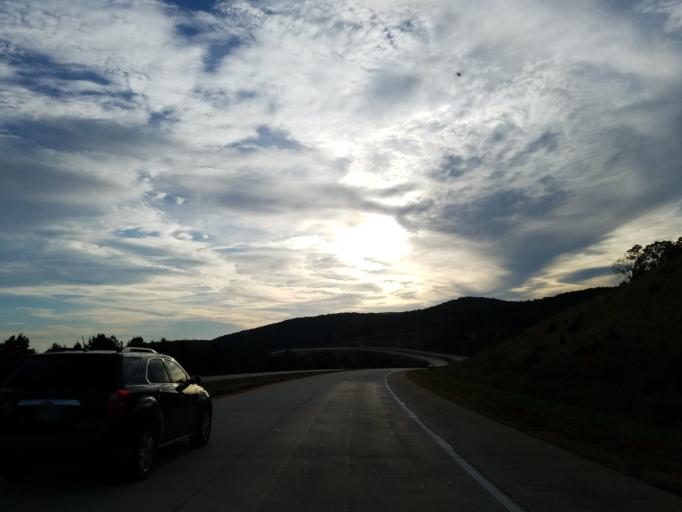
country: US
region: Georgia
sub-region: Bartow County
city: Emerson
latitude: 34.1349
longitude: -84.7552
